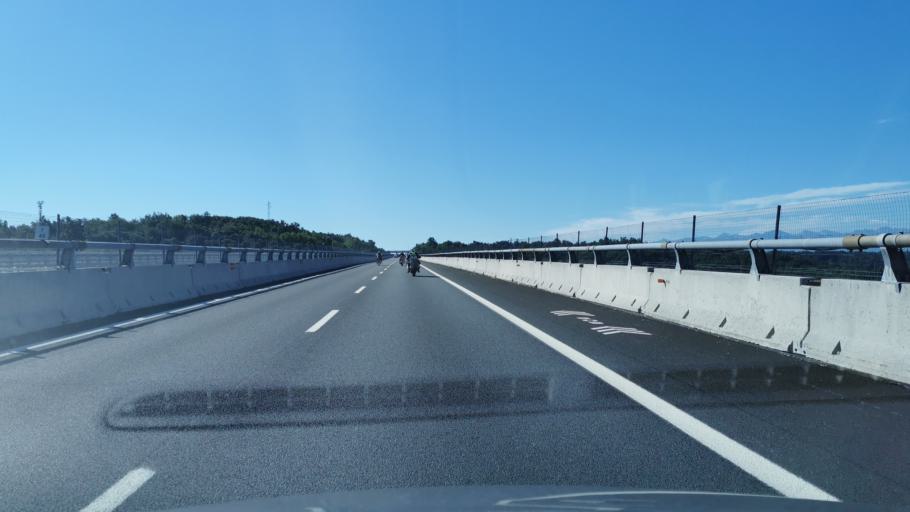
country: IT
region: Piedmont
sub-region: Provincia di Cuneo
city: Salmour
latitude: 44.5733
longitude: 7.7741
